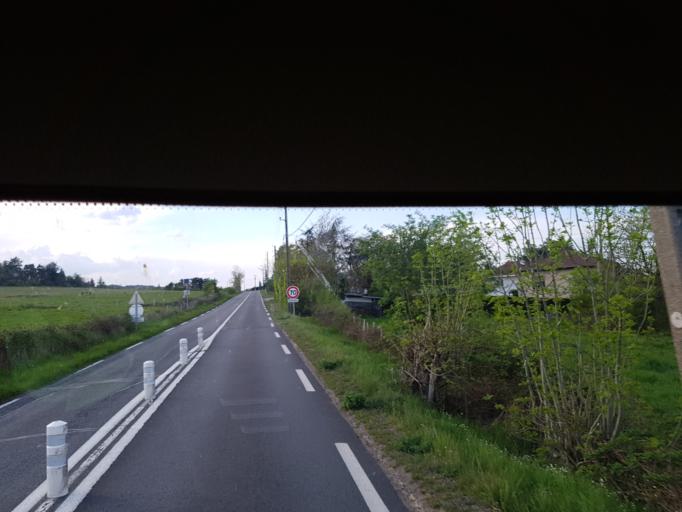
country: FR
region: Rhone-Alpes
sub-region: Departement du Rhone
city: Sainte-Consorce
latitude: 45.7955
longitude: 4.6880
